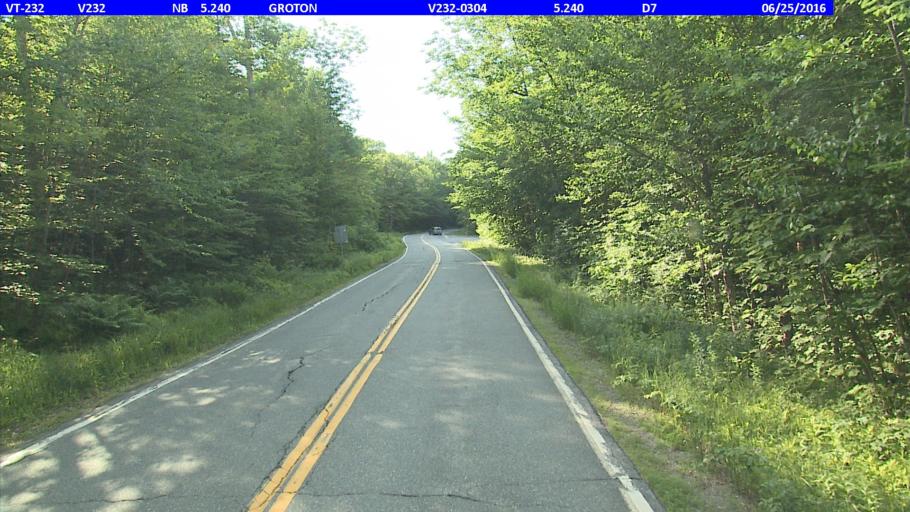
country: US
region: Vermont
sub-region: Washington County
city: Barre
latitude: 44.2756
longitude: -72.2830
